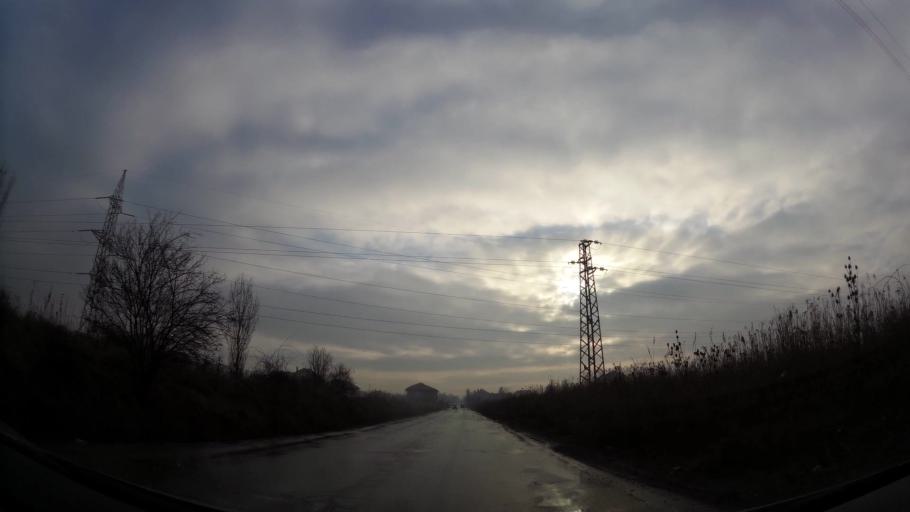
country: BG
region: Sofia-Capital
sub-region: Stolichna Obshtina
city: Sofia
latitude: 42.7385
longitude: 23.3343
